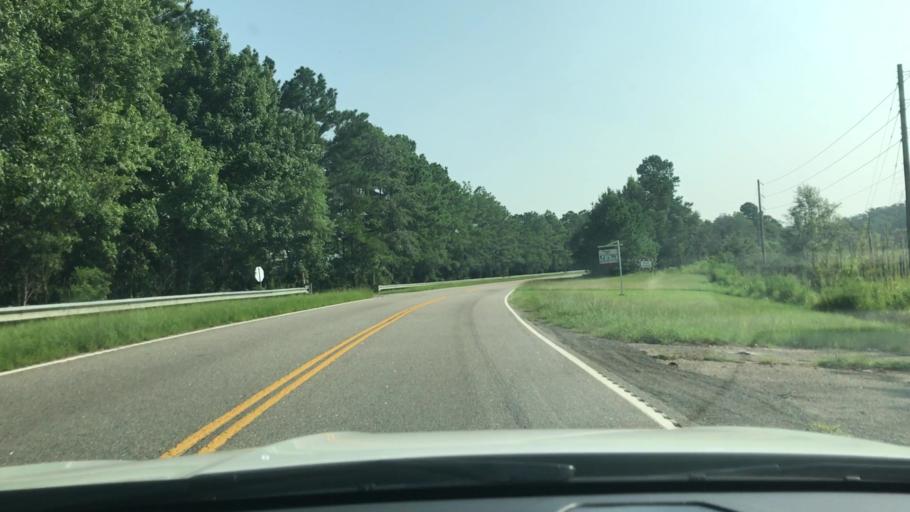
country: US
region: South Carolina
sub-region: Georgetown County
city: Georgetown
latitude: 33.4762
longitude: -79.2781
